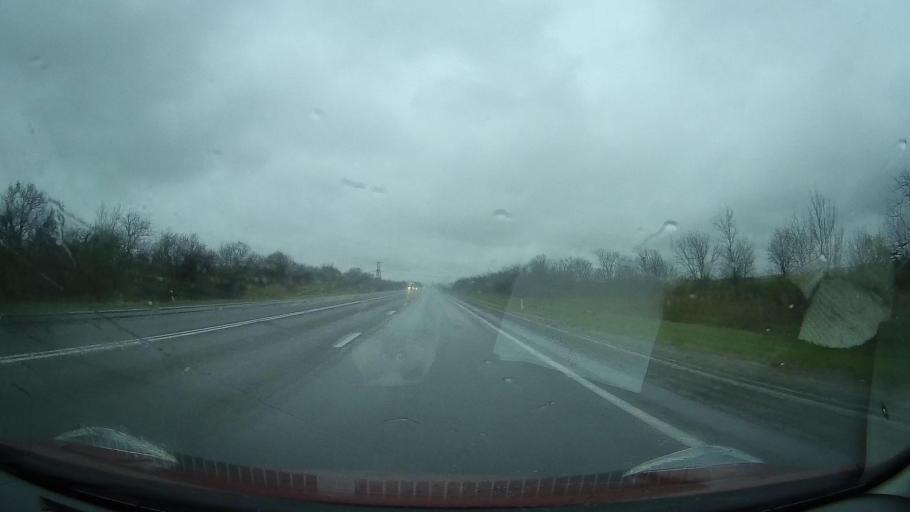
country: RU
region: Stavropol'skiy
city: Nevinnomyssk
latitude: 44.6331
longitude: 42.0139
